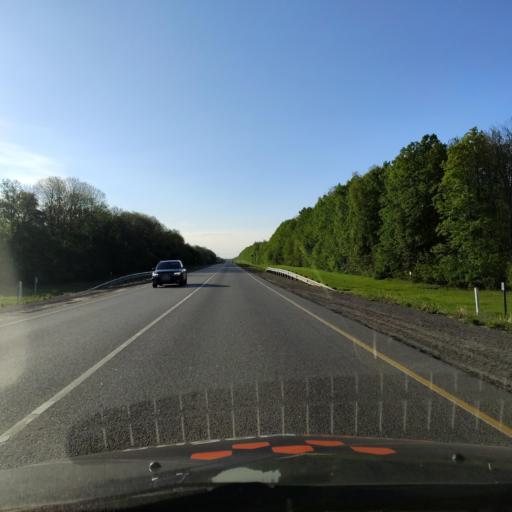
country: RU
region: Lipetsk
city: Yelets
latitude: 52.5722
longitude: 38.6570
